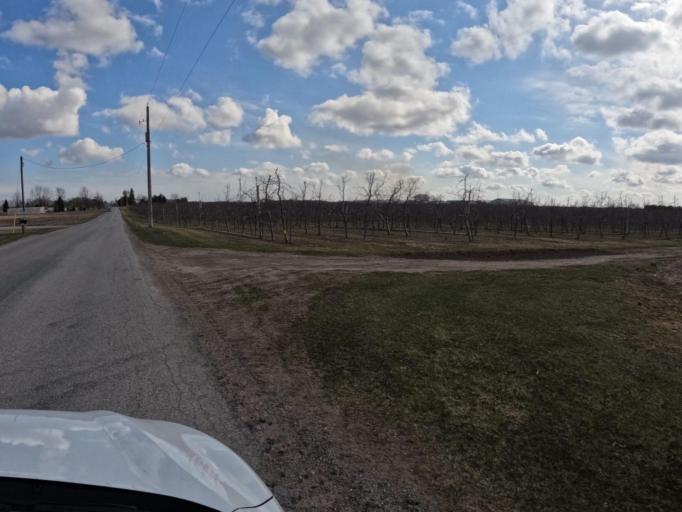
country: CA
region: Ontario
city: Norfolk County
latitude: 42.8814
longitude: -80.2821
